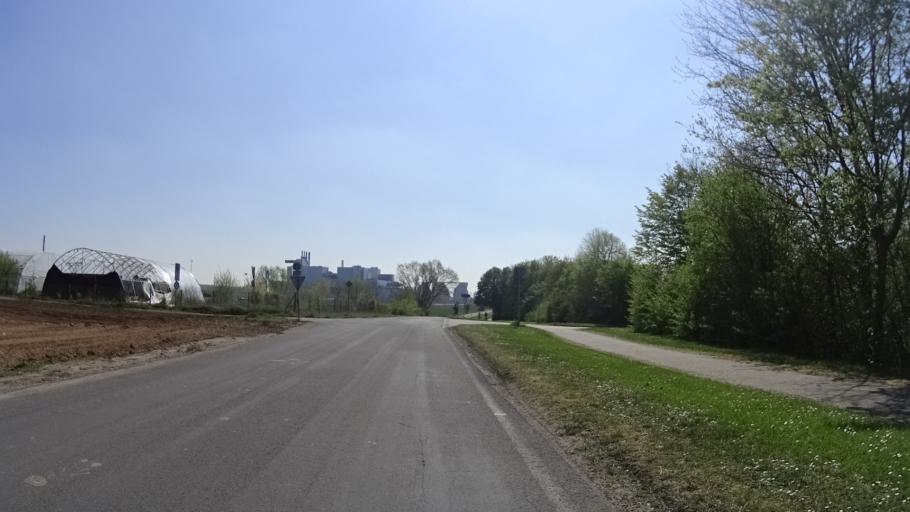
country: DE
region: North Rhine-Westphalia
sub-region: Regierungsbezirk Dusseldorf
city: Krefeld
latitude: 51.3863
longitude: 6.6317
